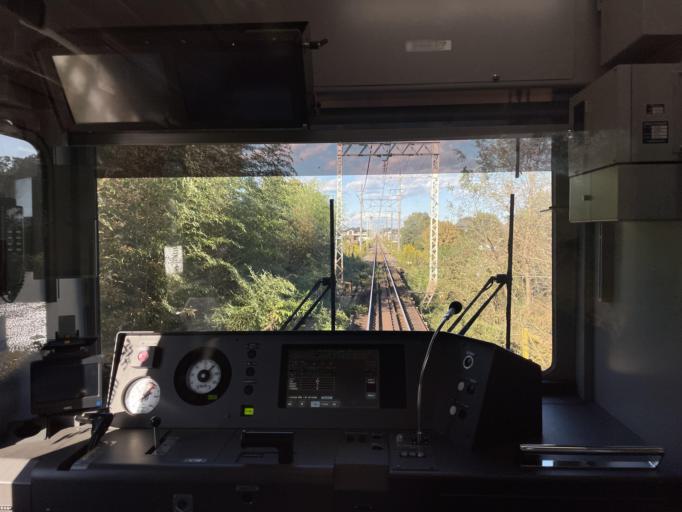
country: JP
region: Tochigi
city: Mibu
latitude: 36.4281
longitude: 139.8086
